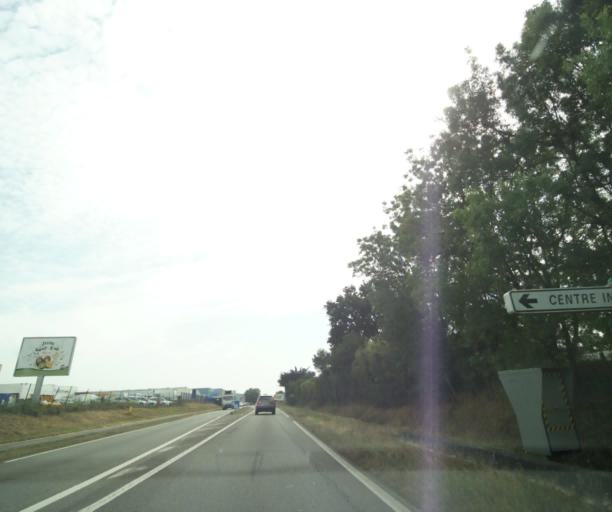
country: FR
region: Pays de la Loire
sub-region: Departement de la Loire-Atlantique
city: Saint-Herblain
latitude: 47.2188
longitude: -1.6500
